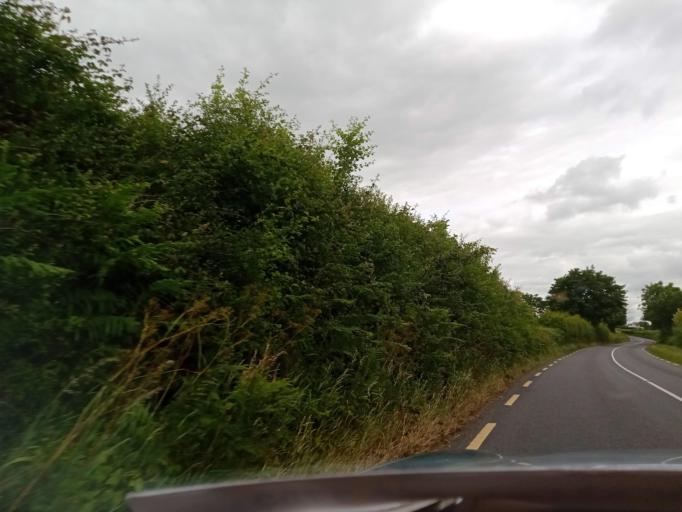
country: IE
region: Leinster
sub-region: Kilkenny
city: Thomastown
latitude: 52.4756
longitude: -7.2601
